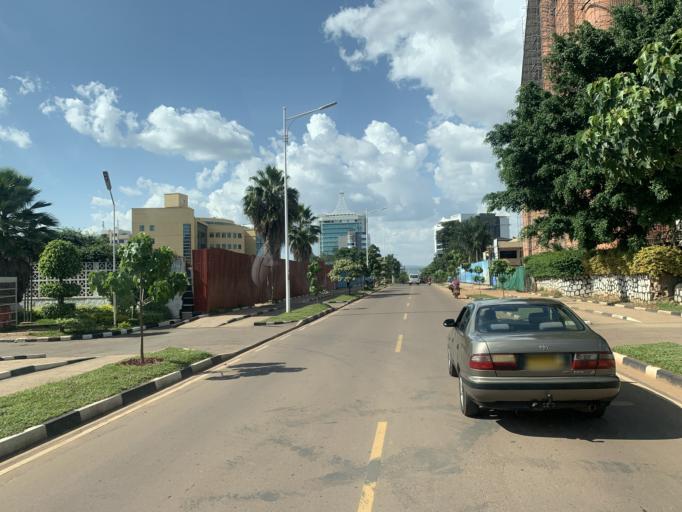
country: RW
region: Kigali
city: Kigali
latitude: -1.9501
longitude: 30.0613
